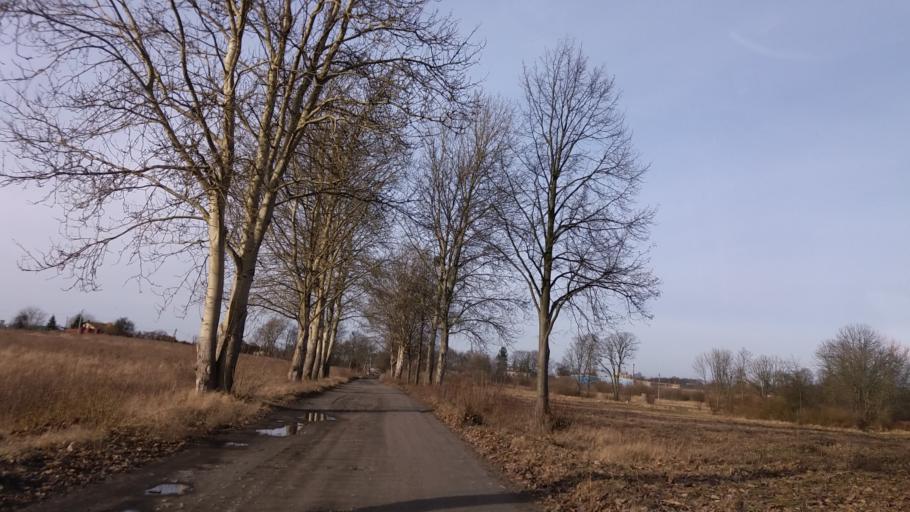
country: PL
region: West Pomeranian Voivodeship
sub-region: Powiat choszczenski
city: Choszczno
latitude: 53.1568
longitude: 15.4051
